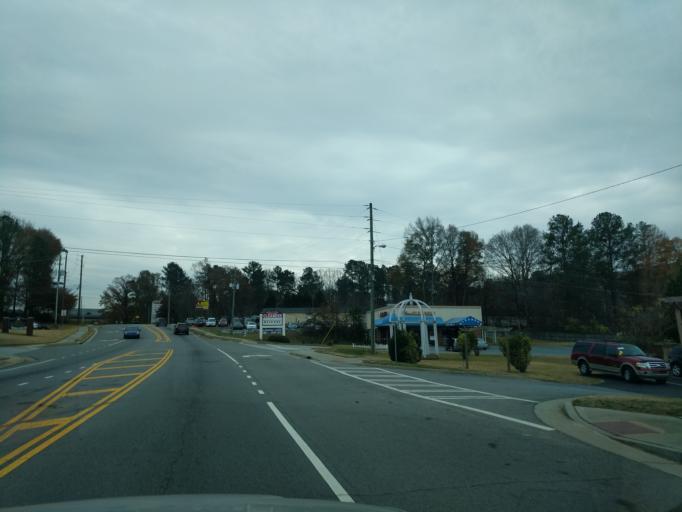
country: US
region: Georgia
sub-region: Gwinnett County
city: Duluth
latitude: 34.0231
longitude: -84.1634
